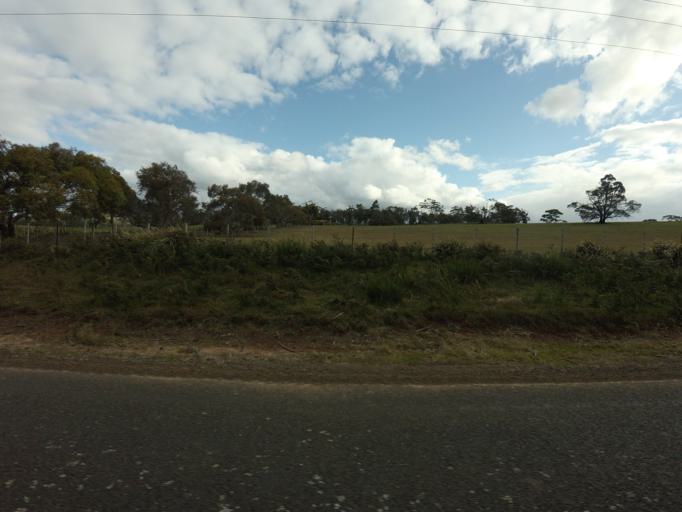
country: AU
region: Tasmania
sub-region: Northern Midlands
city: Evandale
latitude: -41.8738
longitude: 147.3011
